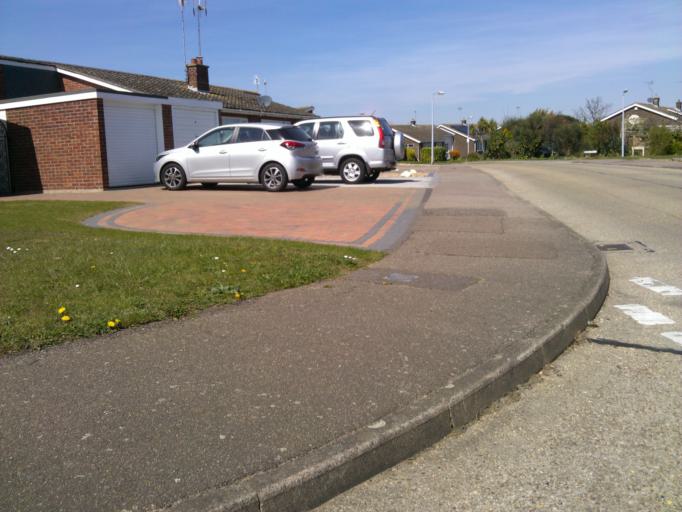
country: GB
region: England
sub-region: Essex
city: Clacton-on-Sea
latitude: 51.8061
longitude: 1.1582
